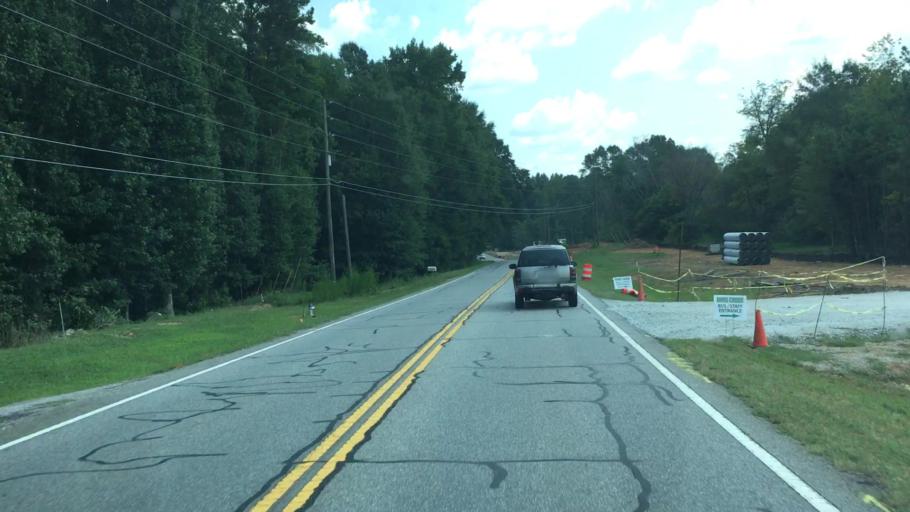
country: US
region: Georgia
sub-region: Barrow County
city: Statham
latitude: 33.9185
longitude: -83.6059
